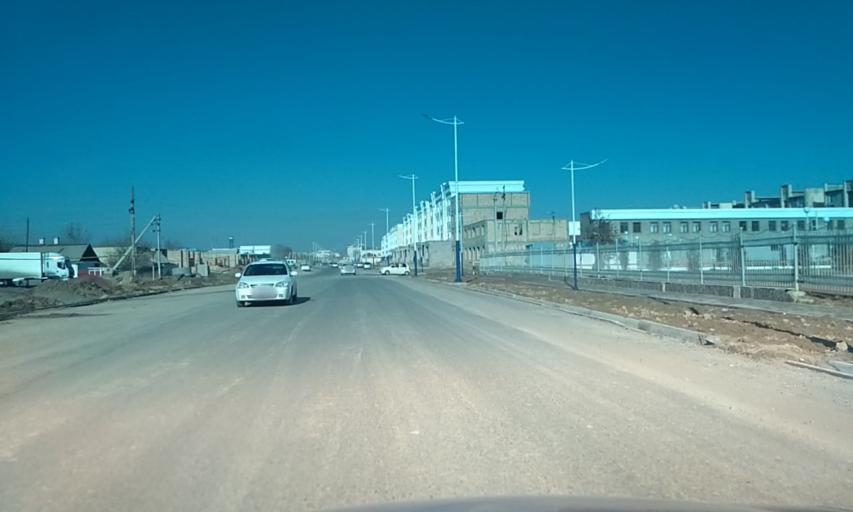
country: UZ
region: Sirdaryo
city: Guliston
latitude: 40.5035
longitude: 68.7713
